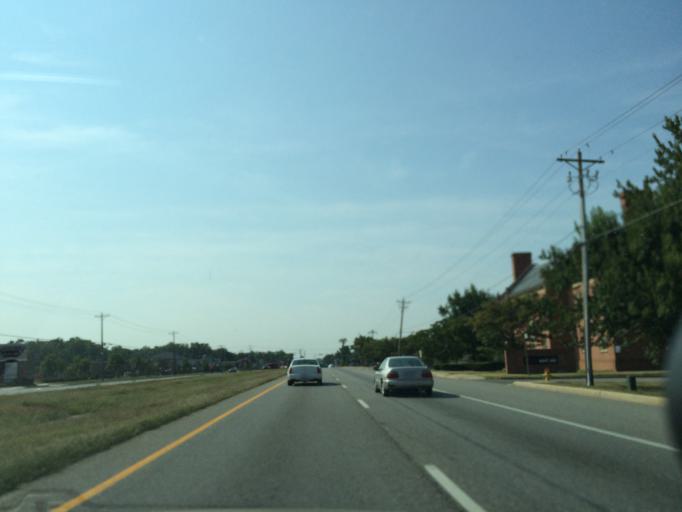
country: US
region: Maryland
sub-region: Charles County
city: La Plata
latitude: 38.5424
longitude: -76.9847
